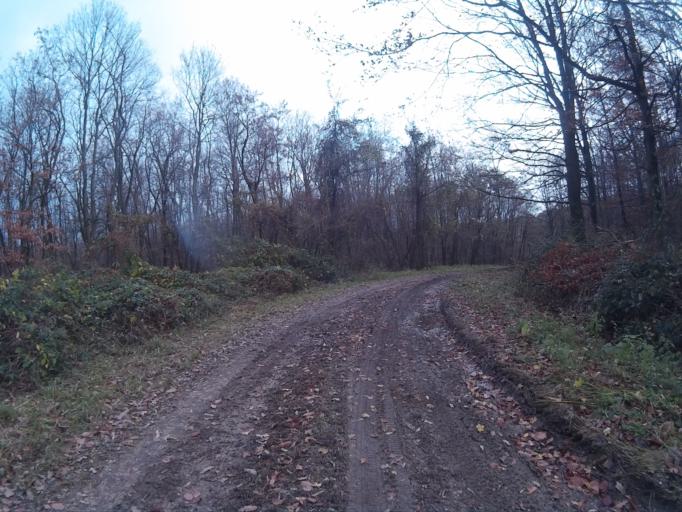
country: HU
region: Veszprem
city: Tapolca
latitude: 46.9816
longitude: 17.5084
